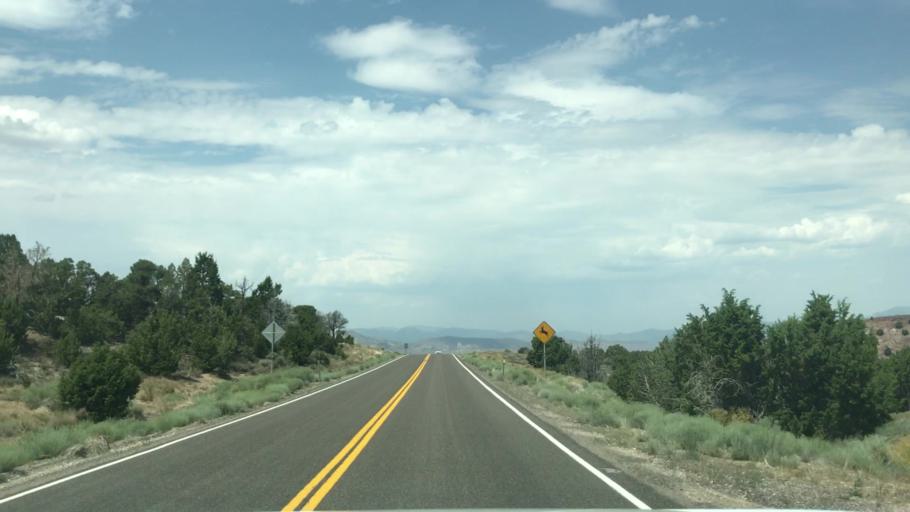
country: US
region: Nevada
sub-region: Eureka County
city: Eureka
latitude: 39.3915
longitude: -115.5059
